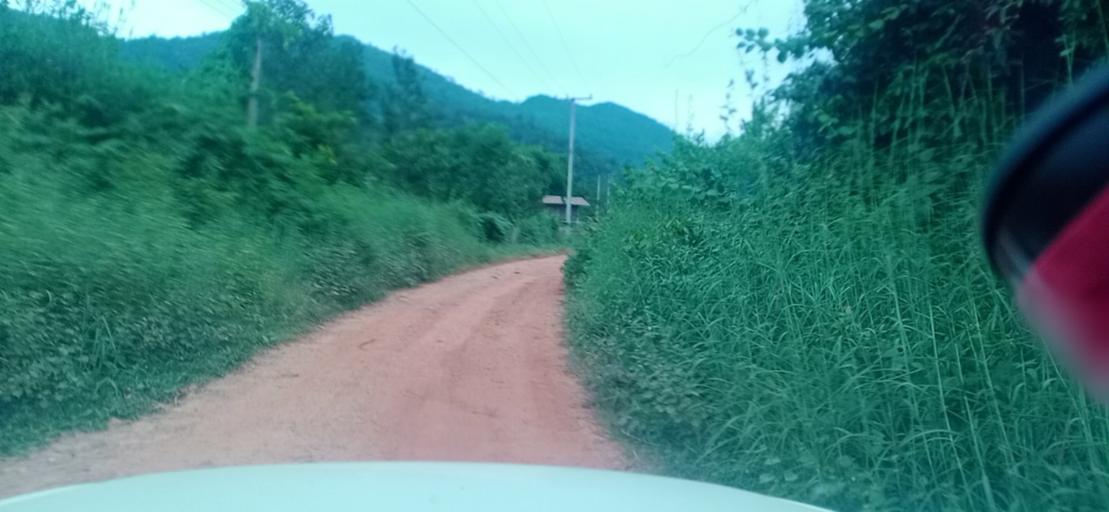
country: TH
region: Changwat Bueng Kan
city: Pak Khat
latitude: 18.5667
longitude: 103.3078
